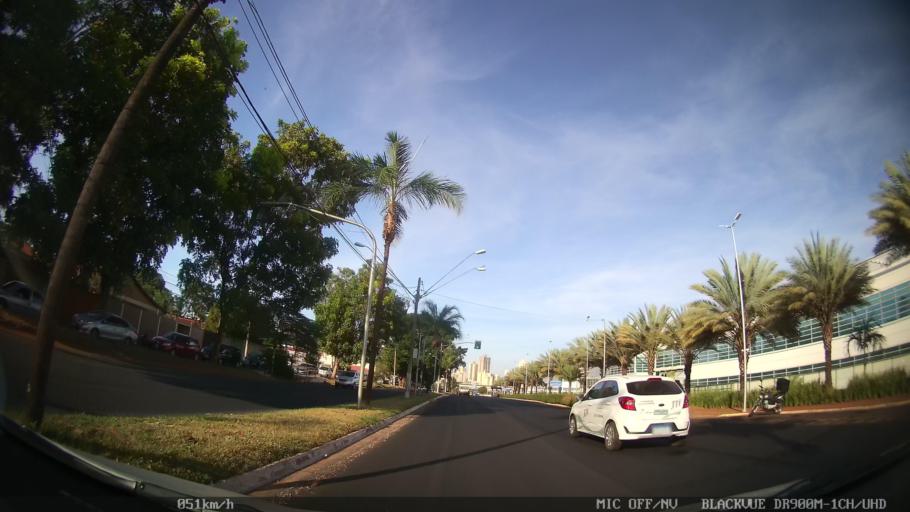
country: BR
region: Sao Paulo
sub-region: Ribeirao Preto
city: Ribeirao Preto
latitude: -21.2117
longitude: -47.8137
